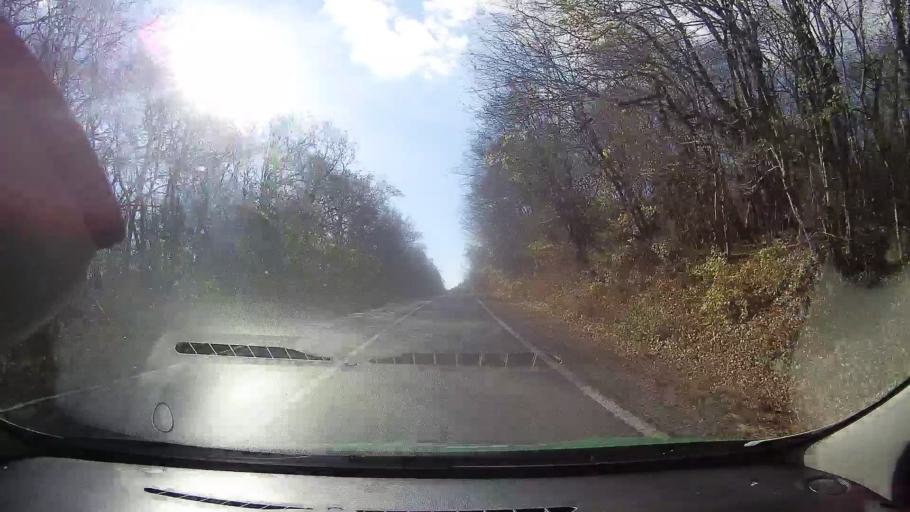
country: RO
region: Tulcea
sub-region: Oras Babadag
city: Babadag
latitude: 44.8420
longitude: 28.6974
